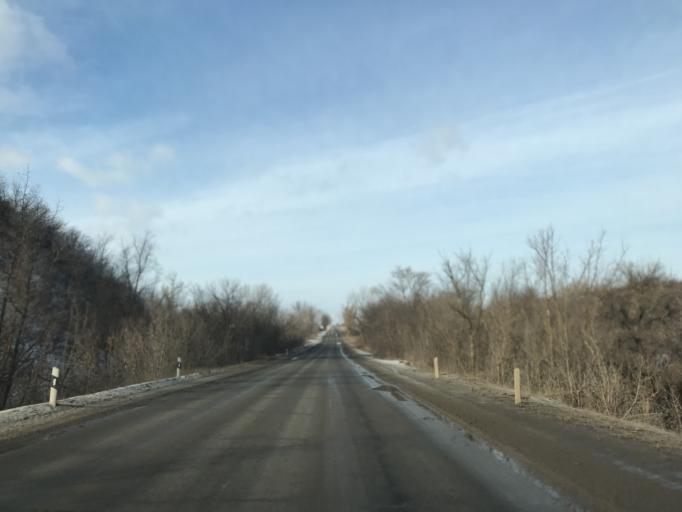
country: RU
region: Rostov
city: Staraya Stanitsa
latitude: 48.2391
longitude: 40.4025
